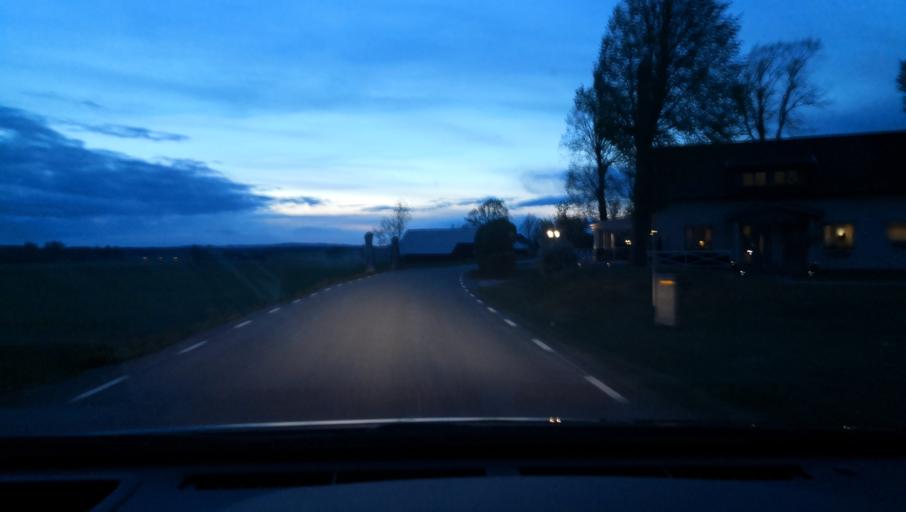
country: SE
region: OErebro
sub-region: Orebro Kommun
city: Vintrosa
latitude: 59.1519
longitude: 15.0046
